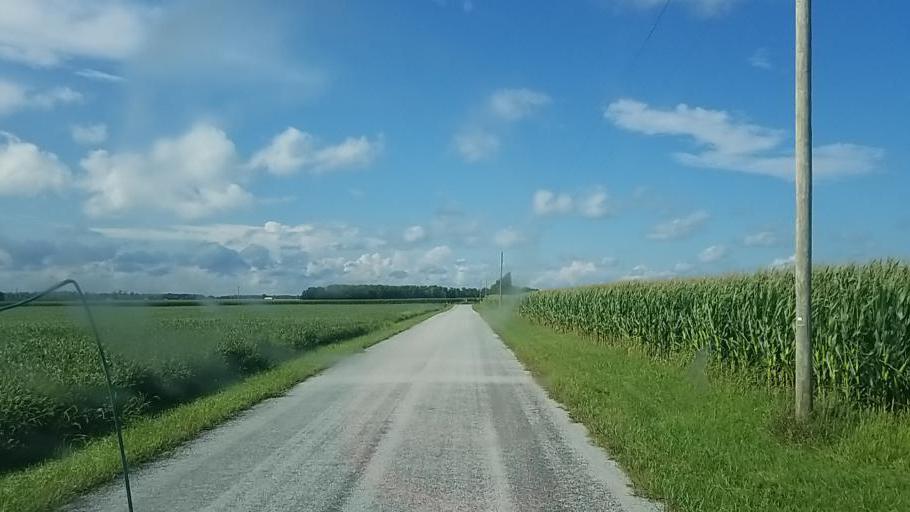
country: US
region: Ohio
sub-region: Hardin County
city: Kenton
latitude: 40.6995
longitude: -83.5309
